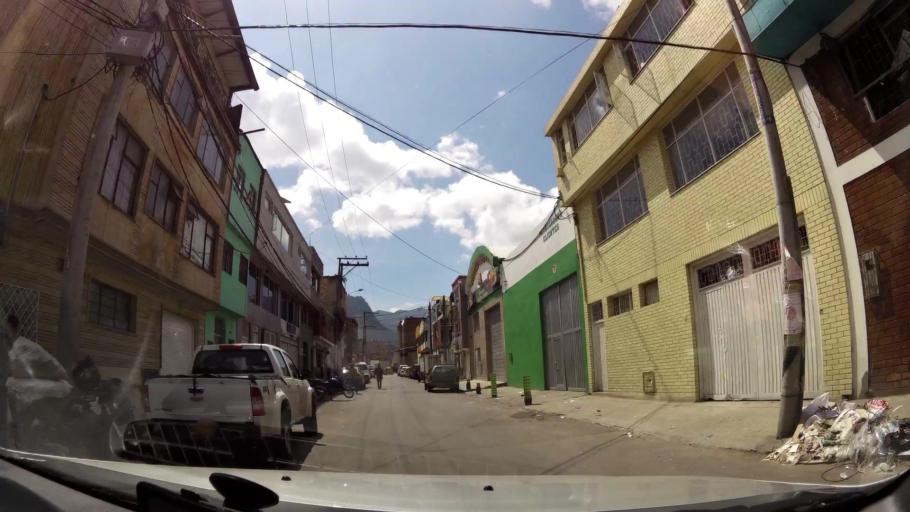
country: CO
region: Bogota D.C.
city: Bogota
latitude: 4.6172
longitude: -74.0824
